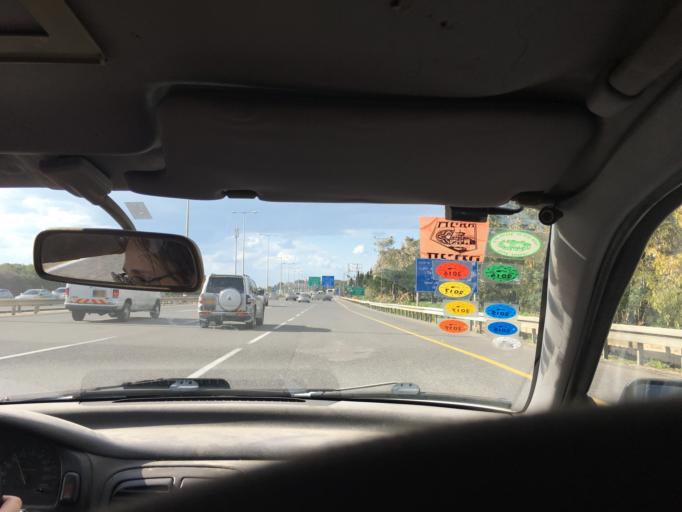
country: IL
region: Tel Aviv
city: Ramat HaSharon
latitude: 32.1373
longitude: 34.8274
